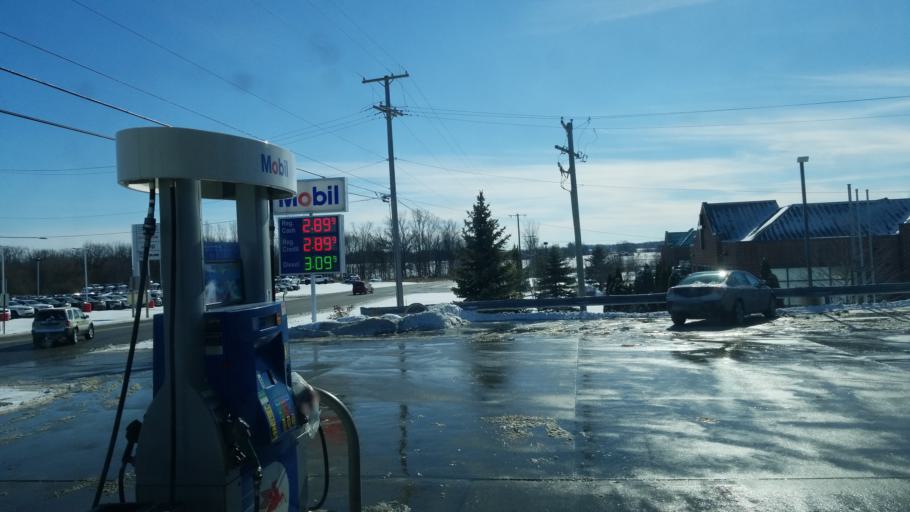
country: US
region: Michigan
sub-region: Livingston County
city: Fowlerville
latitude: 42.6447
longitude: -84.0729
